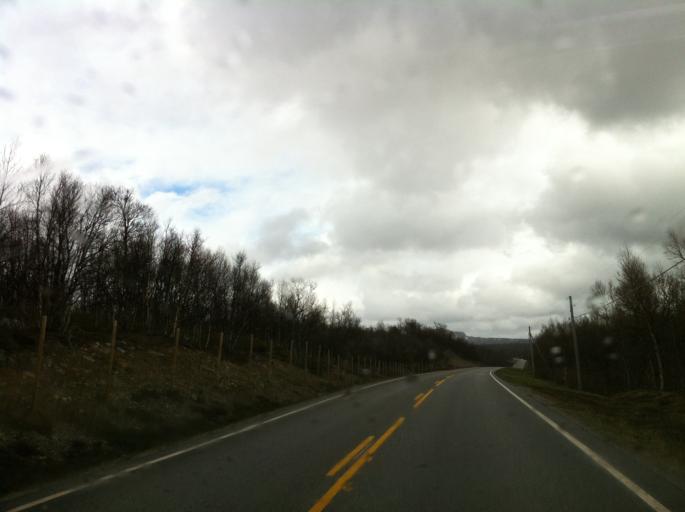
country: NO
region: Sor-Trondelag
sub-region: Tydal
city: Aas
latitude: 62.6443
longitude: 11.8819
